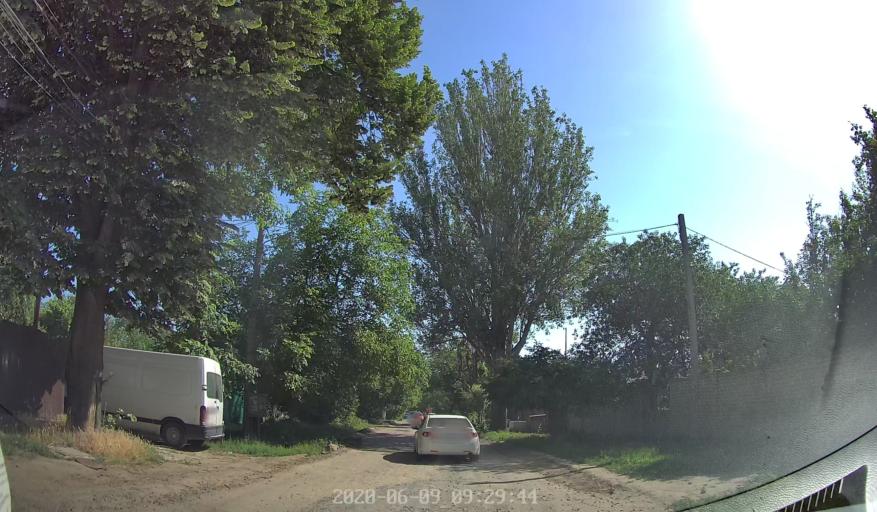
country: NE
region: Zinder
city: Mirriah
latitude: 13.9273
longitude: 9.2192
